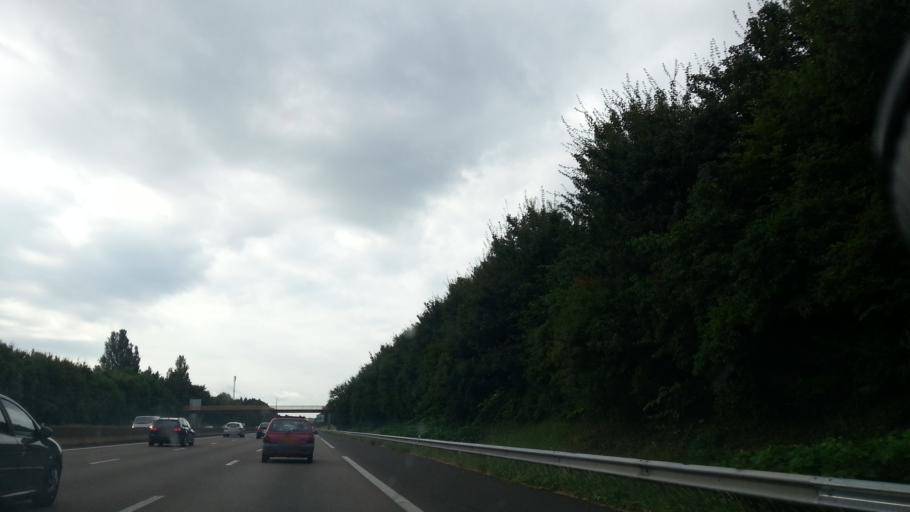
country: FR
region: Bourgogne
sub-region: Departement de Saone-et-Loire
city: Saint-Remy
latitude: 46.7654
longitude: 4.8240
